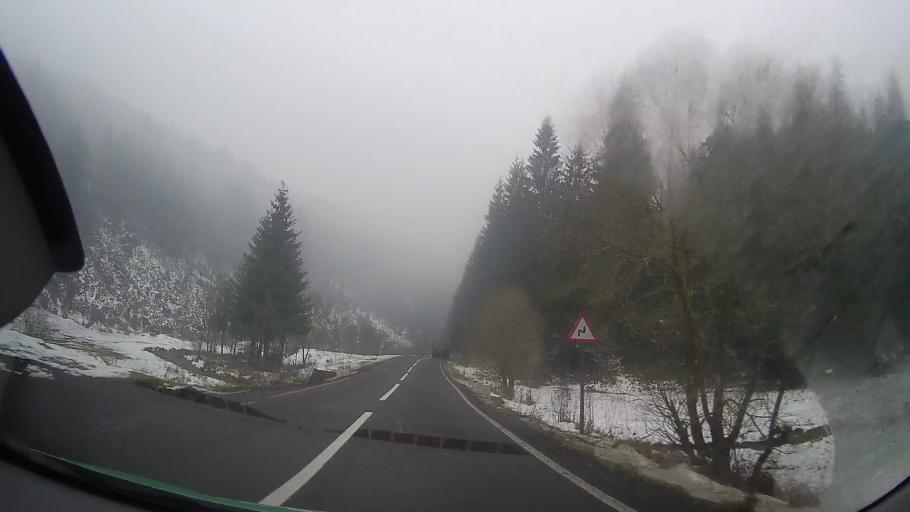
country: RO
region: Harghita
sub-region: Municipiul Gheorgheni
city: Gheorgheni
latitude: 46.7567
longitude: 25.6969
